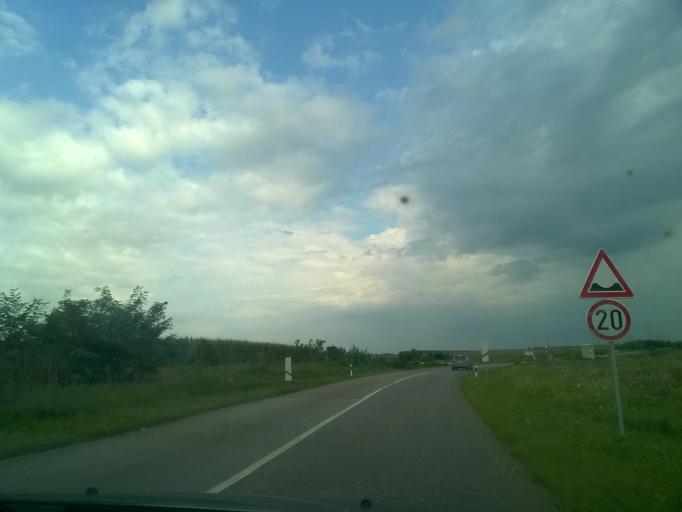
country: RS
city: Uzdin
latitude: 45.2283
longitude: 20.6261
